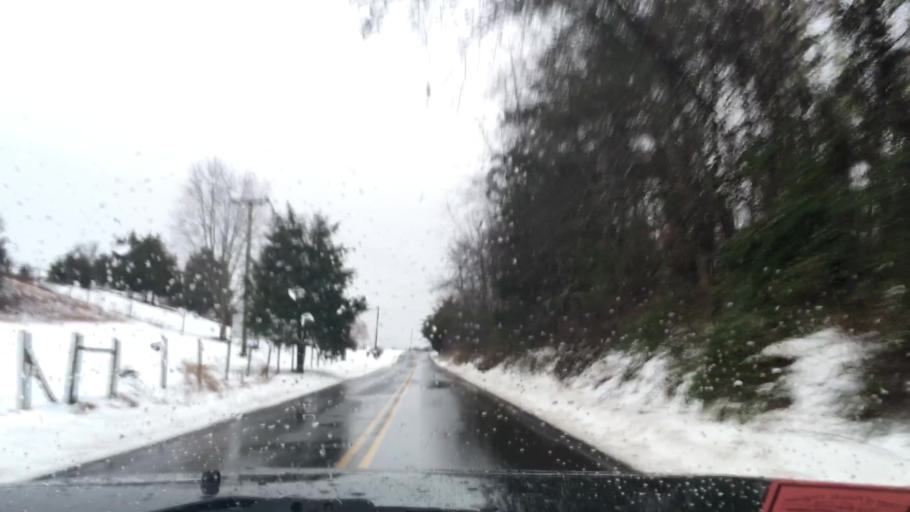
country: US
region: Virginia
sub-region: Pulaski County
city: Dublin
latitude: 37.0164
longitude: -80.6423
